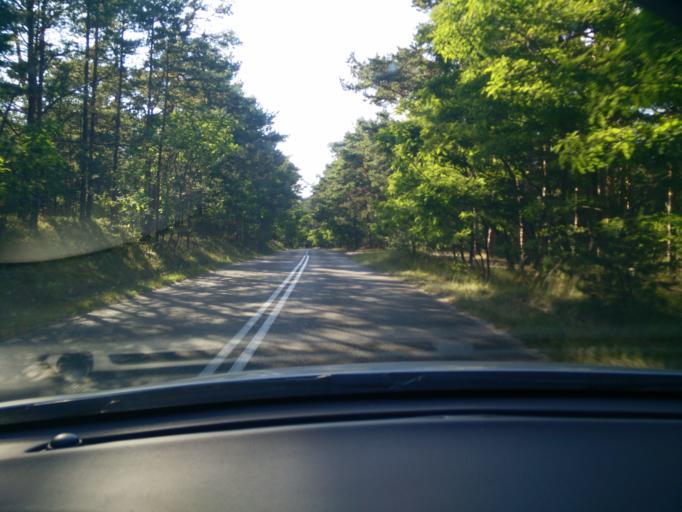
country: PL
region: Pomeranian Voivodeship
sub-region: Powiat pucki
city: Jastarnia
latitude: 54.6698
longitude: 18.7390
